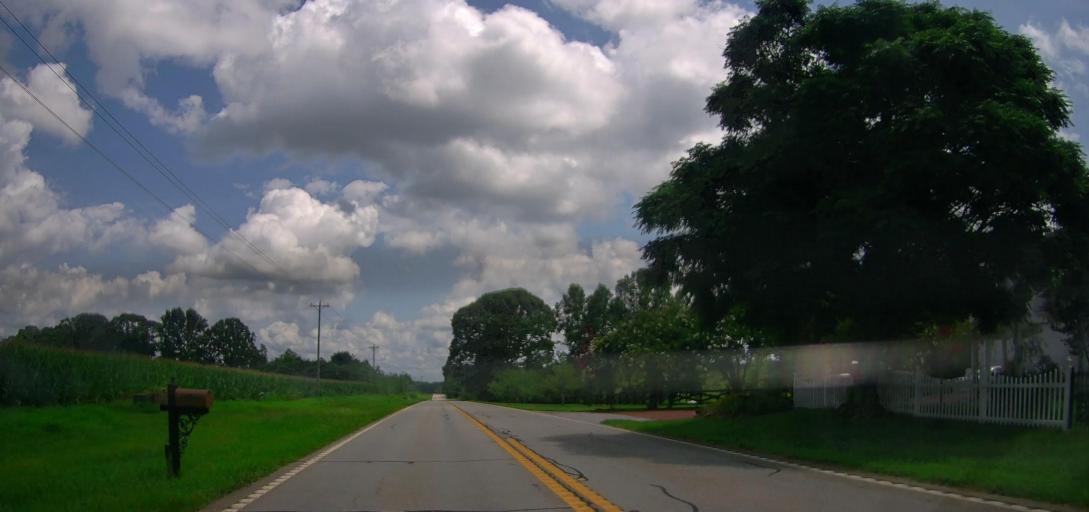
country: US
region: Georgia
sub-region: Heard County
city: Franklin
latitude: 33.3544
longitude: -85.1931
